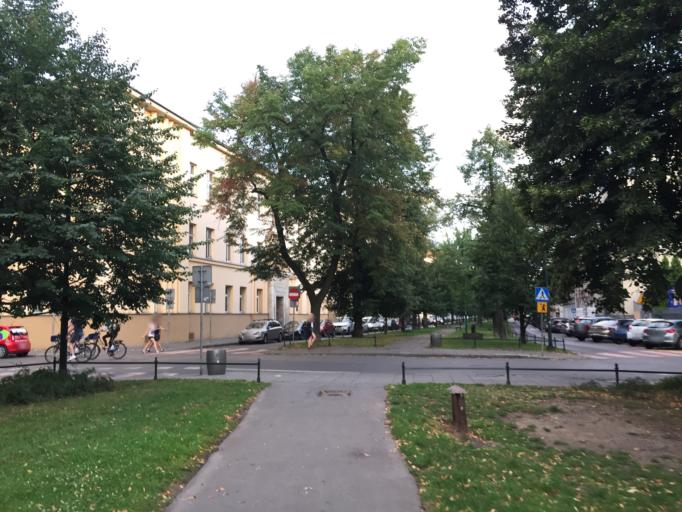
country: PL
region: Lesser Poland Voivodeship
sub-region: Krakow
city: Krakow
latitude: 50.0589
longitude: 19.9283
